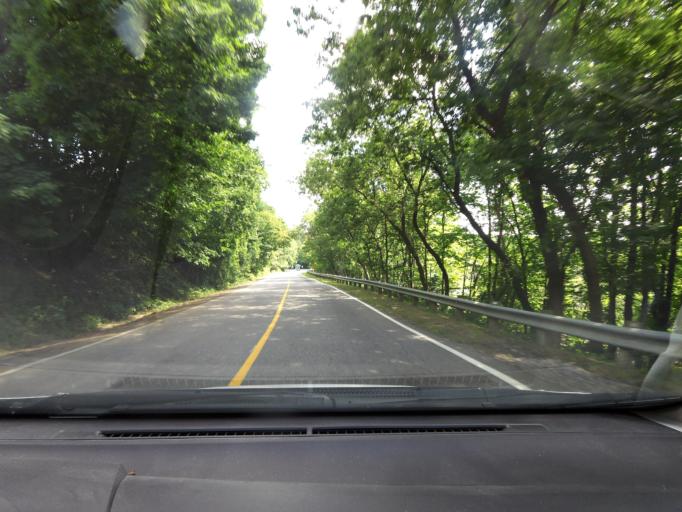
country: CA
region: Quebec
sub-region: Capitale-Nationale
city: Neuville
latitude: 46.7173
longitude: -71.5475
